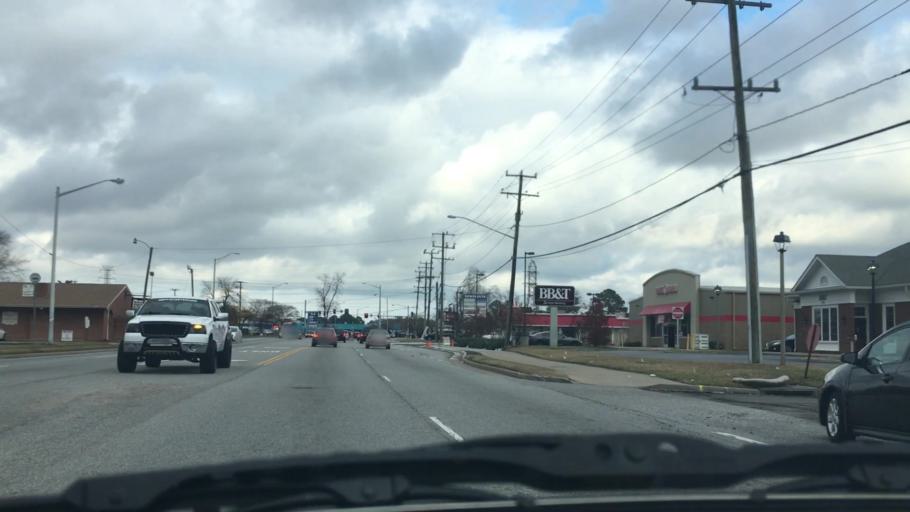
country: US
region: Virginia
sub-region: City of Chesapeake
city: Chesapeake
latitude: 36.8577
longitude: -76.1766
